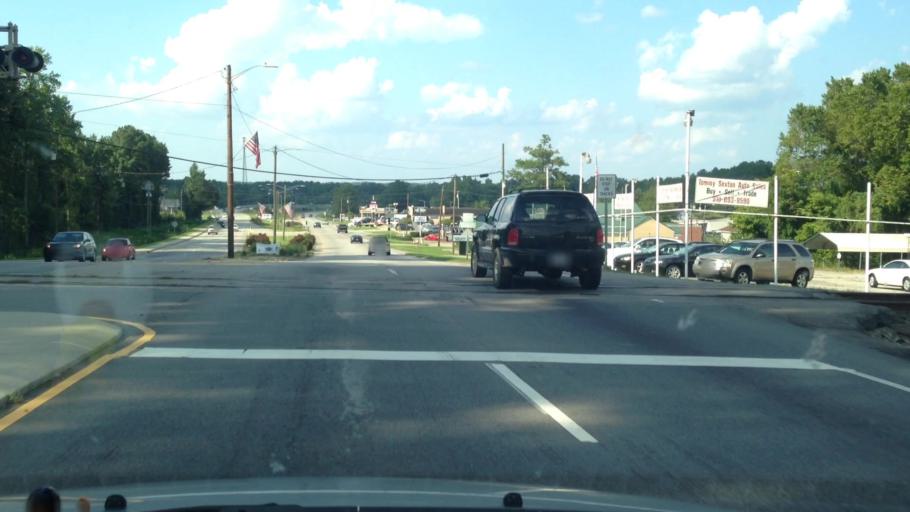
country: US
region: North Carolina
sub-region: Harnett County
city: Lillington
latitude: 35.4006
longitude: -78.8154
